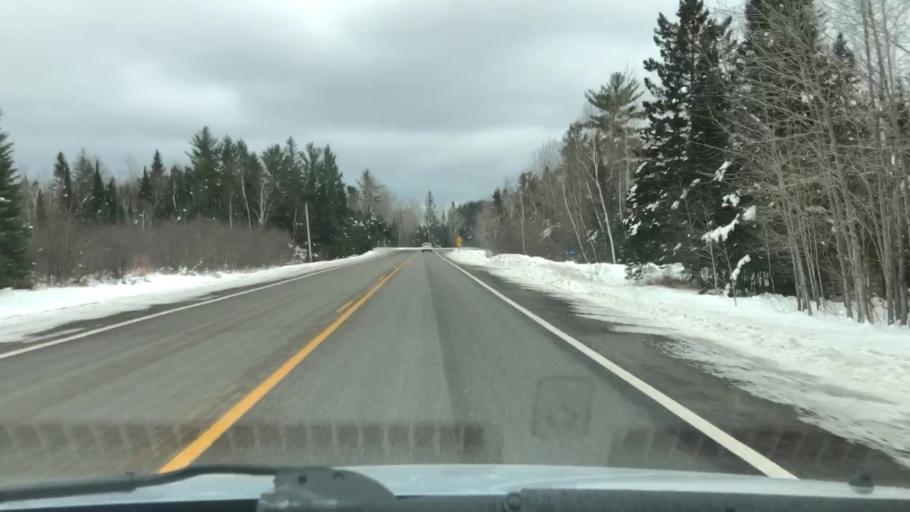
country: US
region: Minnesota
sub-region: Carlton County
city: Esko
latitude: 46.6868
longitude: -92.3648
